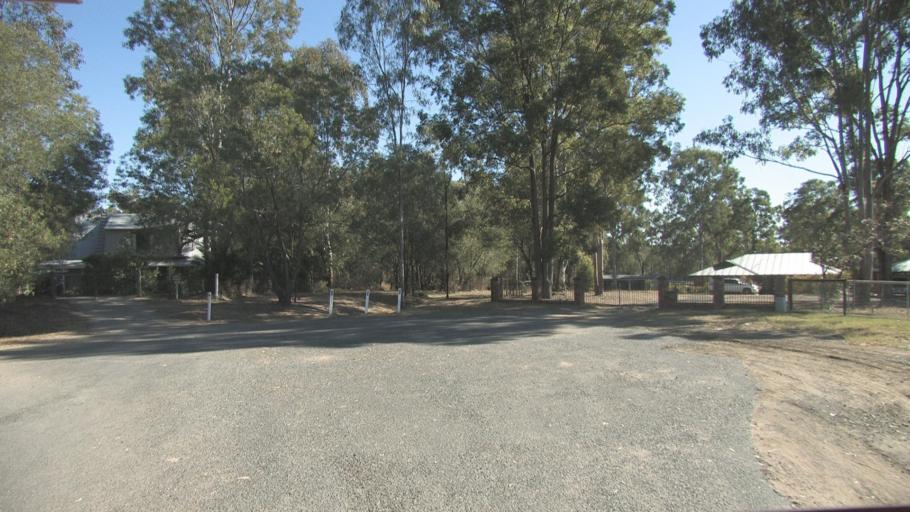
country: AU
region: Queensland
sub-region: Logan
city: North Maclean
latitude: -27.8272
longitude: 152.9383
